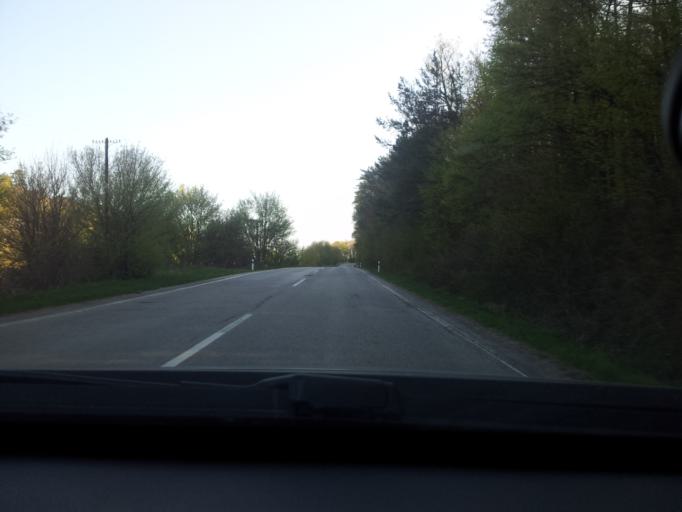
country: SK
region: Nitriansky
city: Zlate Moravce
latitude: 48.4947
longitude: 18.4223
